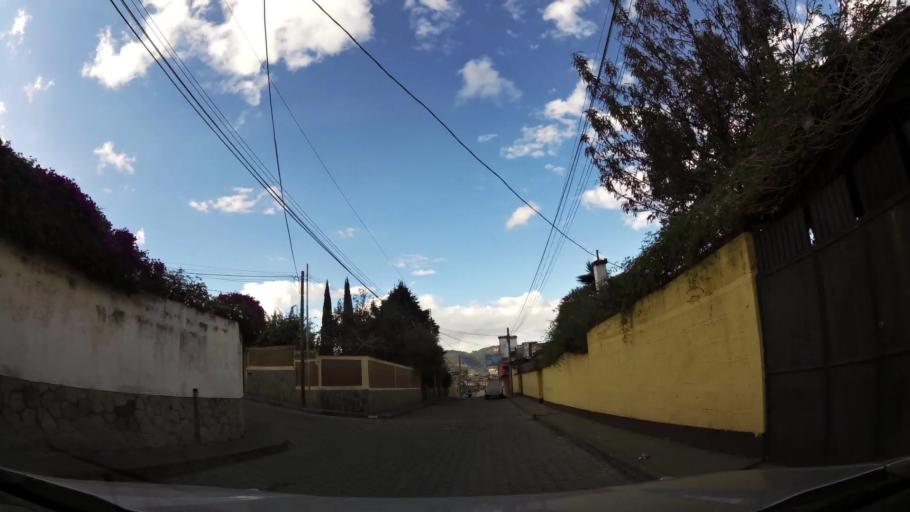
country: GT
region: Quetzaltenango
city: Quetzaltenango
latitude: 14.8526
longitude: -91.5263
